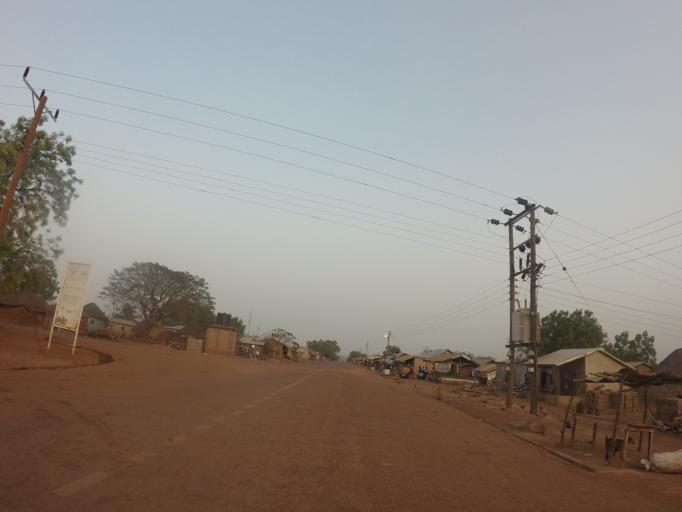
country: GH
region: Northern
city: Tamale
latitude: 9.4455
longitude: -1.1176
